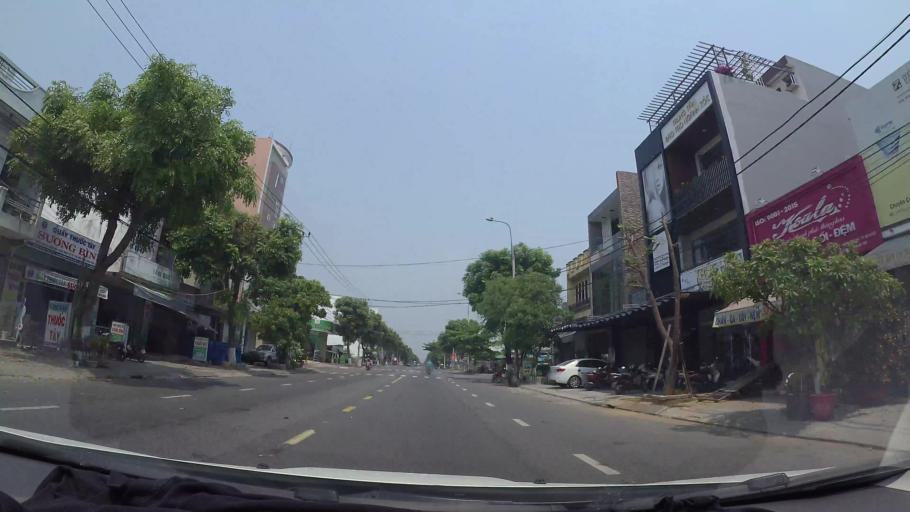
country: VN
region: Da Nang
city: Cam Le
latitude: 15.9860
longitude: 108.2079
